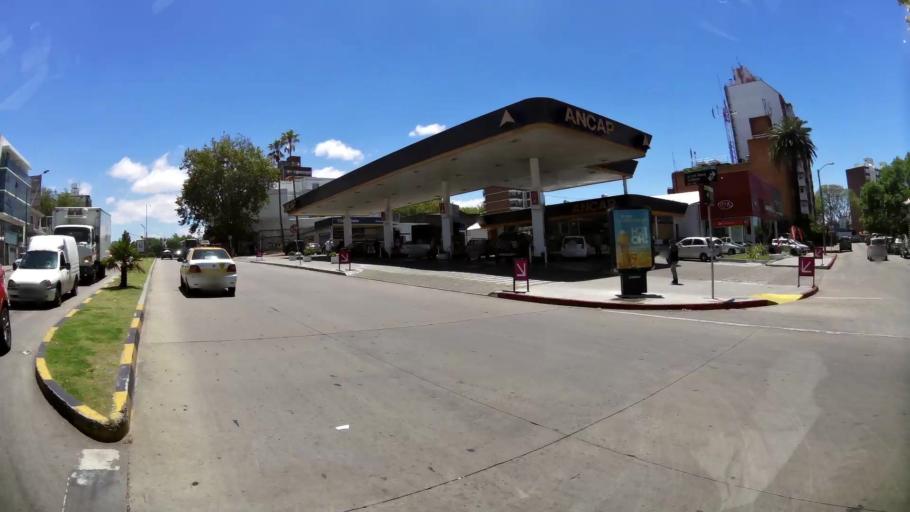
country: UY
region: Montevideo
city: Montevideo
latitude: -34.9022
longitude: -56.1381
